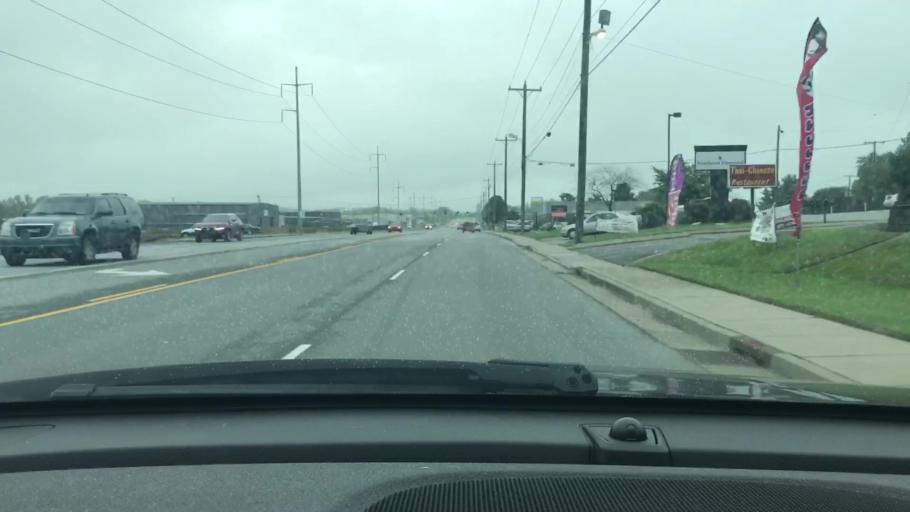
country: US
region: Tennessee
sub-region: Rutherford County
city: La Vergne
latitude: 36.0120
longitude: -86.5940
